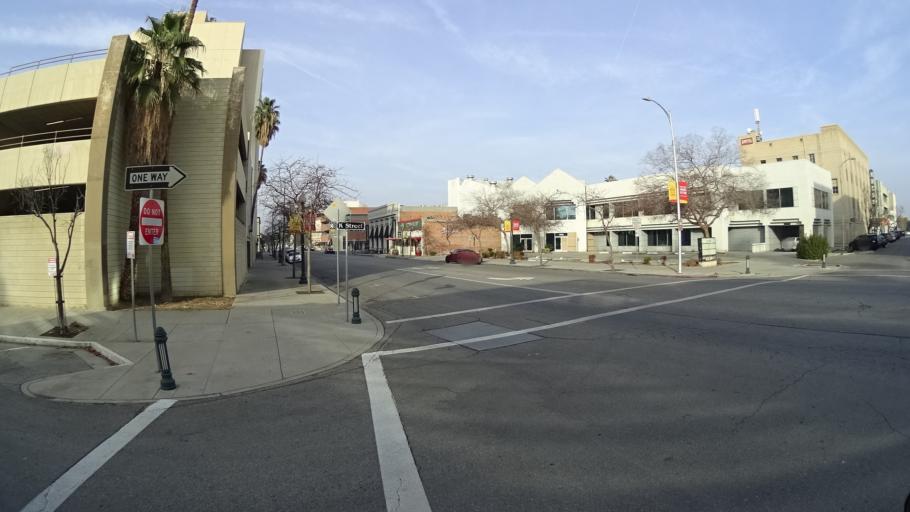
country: US
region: California
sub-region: Kern County
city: Bakersfield
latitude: 35.3752
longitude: -119.0176
